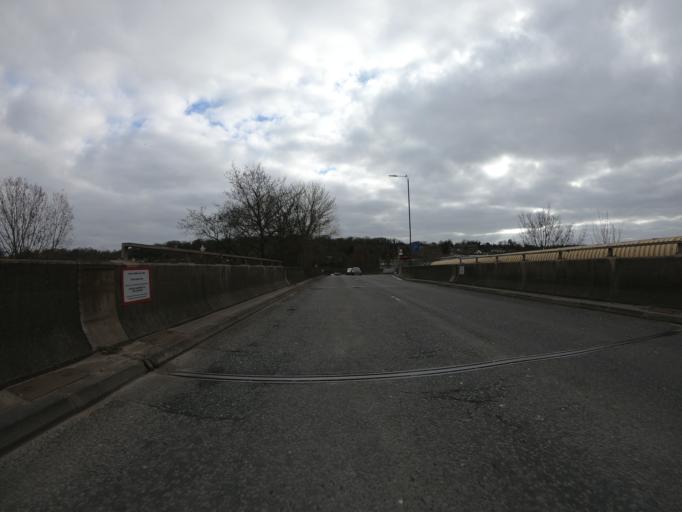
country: GB
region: England
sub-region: Greater London
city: Belvedere
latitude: 51.4922
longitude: 0.1560
